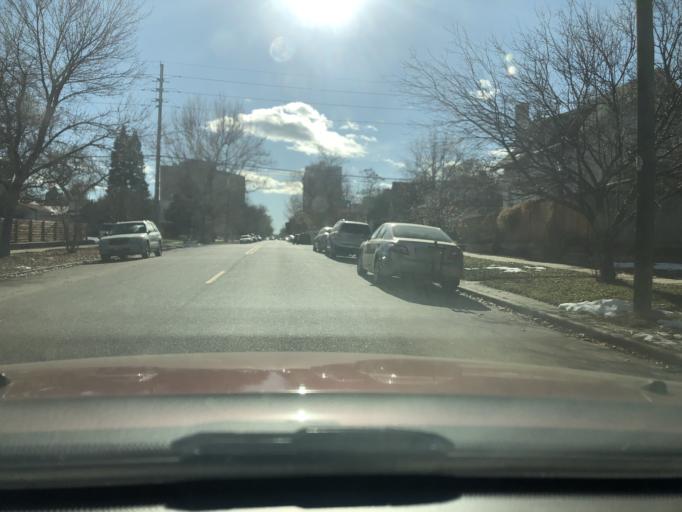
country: US
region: Colorado
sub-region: Denver County
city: Denver
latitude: 39.7512
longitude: -104.9685
